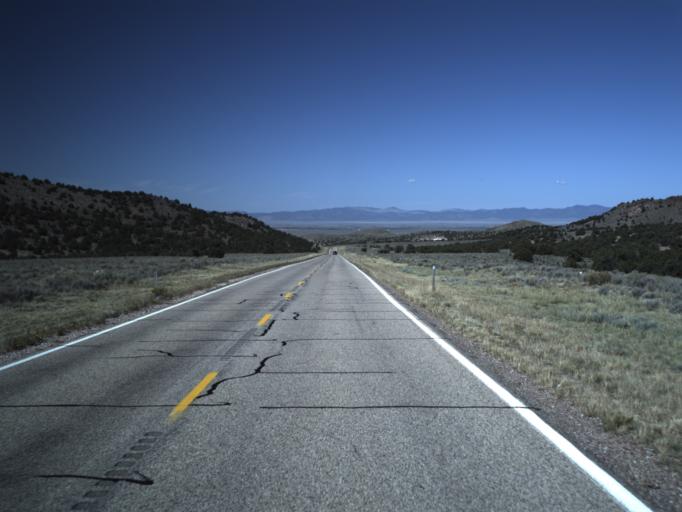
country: US
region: Utah
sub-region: Washington County
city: Enterprise
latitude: 37.6693
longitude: -113.4819
